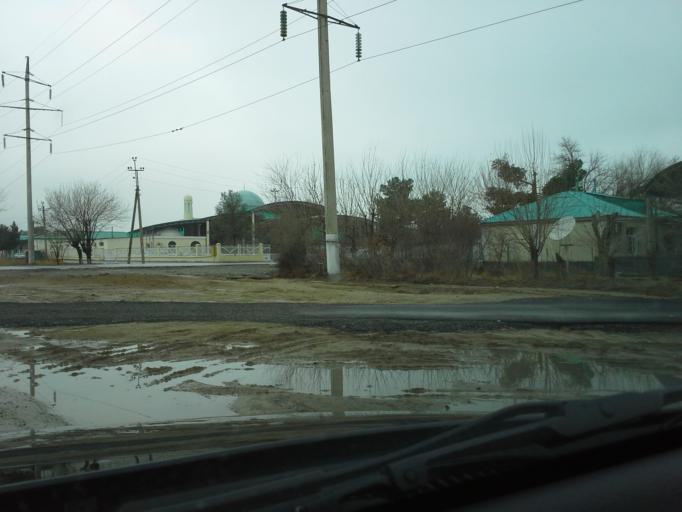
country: TM
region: Ahal
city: Ashgabat
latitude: 37.9522
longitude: 58.4200
